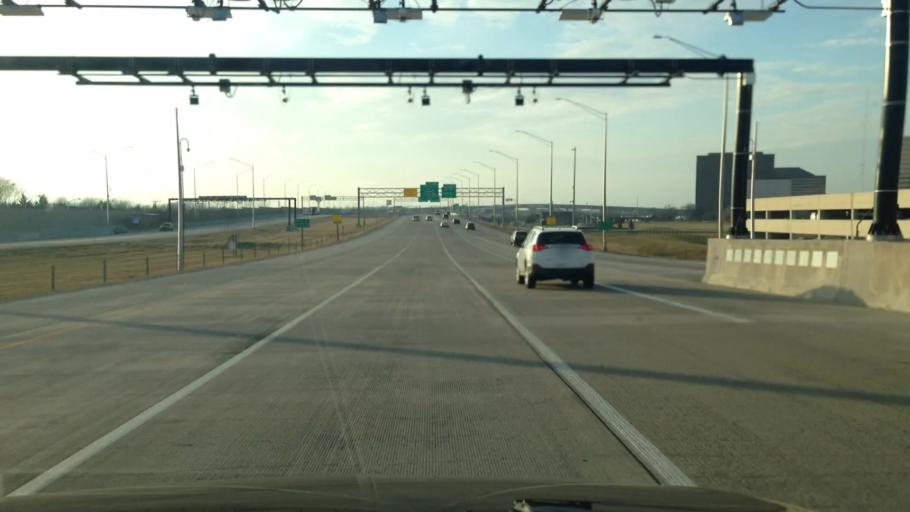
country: US
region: Illinois
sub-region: DuPage County
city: Itasca
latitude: 41.9843
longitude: -88.0071
